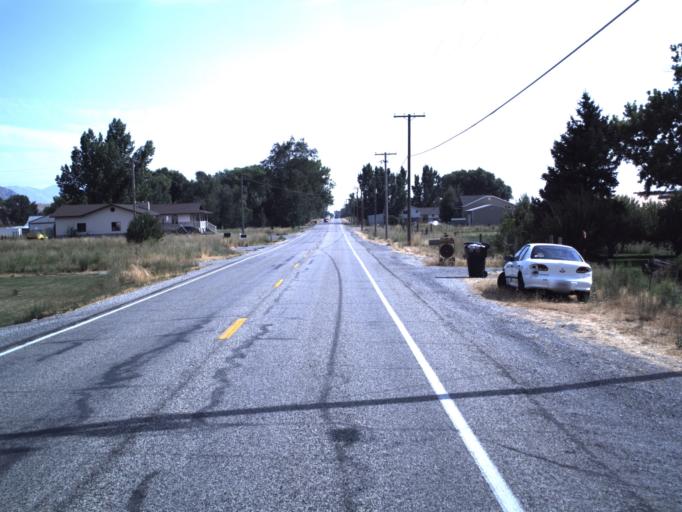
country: US
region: Utah
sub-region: Box Elder County
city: Elwood
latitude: 41.6980
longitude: -112.0901
